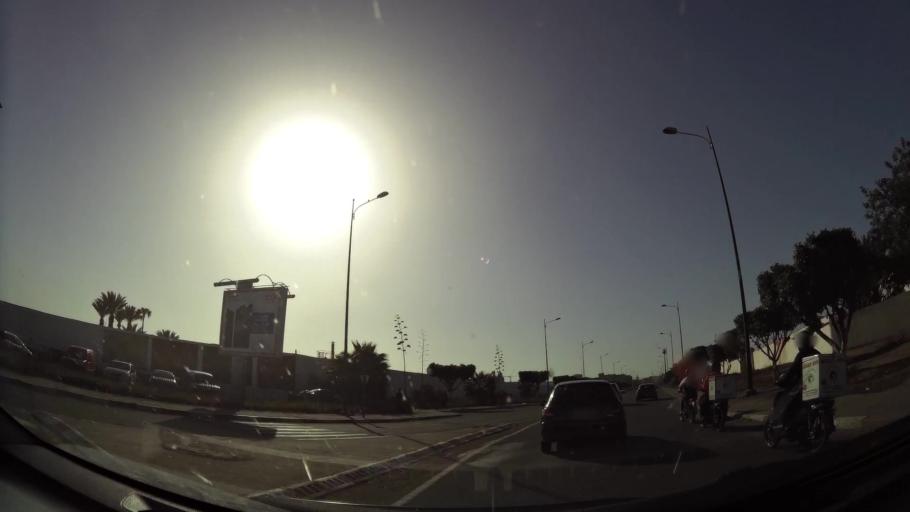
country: MA
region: Oued ed Dahab-Lagouira
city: Dakhla
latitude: 30.3909
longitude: -9.5295
